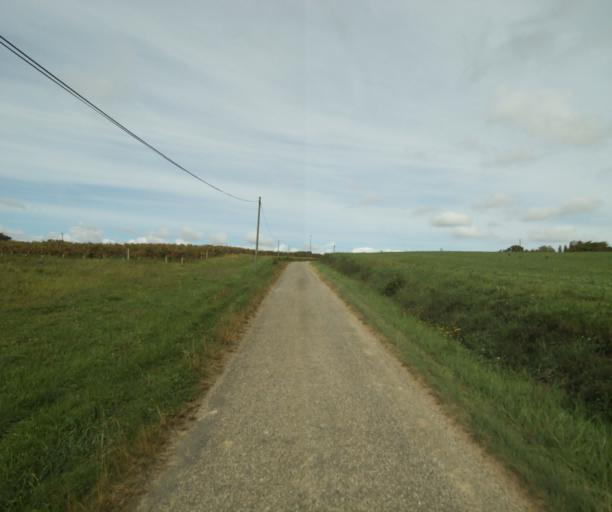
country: FR
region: Midi-Pyrenees
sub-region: Departement du Gers
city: Eauze
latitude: 43.8418
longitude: 0.1414
